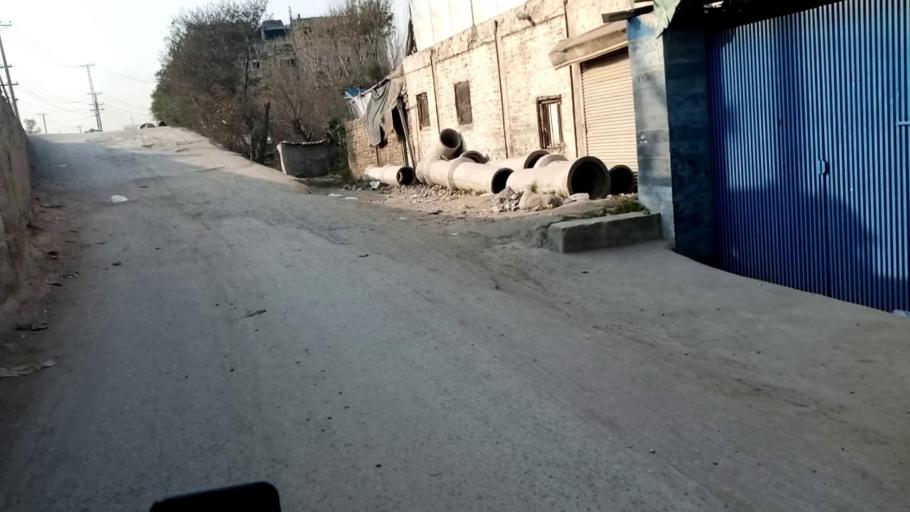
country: PK
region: Khyber Pakhtunkhwa
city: Peshawar
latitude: 34.0046
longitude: 71.4655
